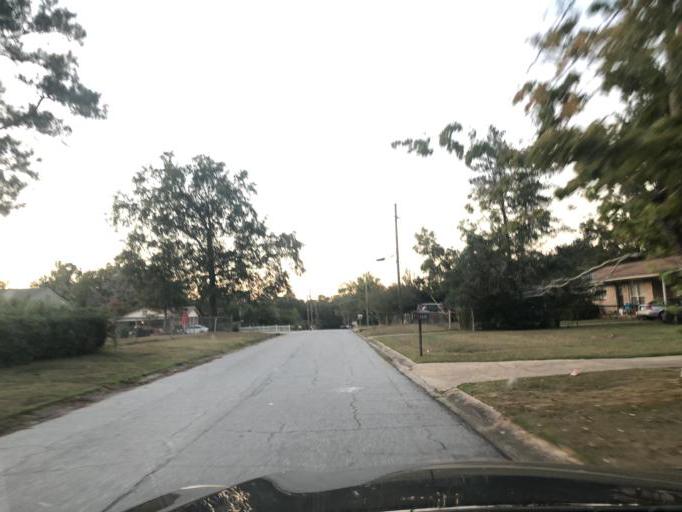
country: US
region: Georgia
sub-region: Muscogee County
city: Columbus
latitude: 32.4663
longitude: -84.8959
